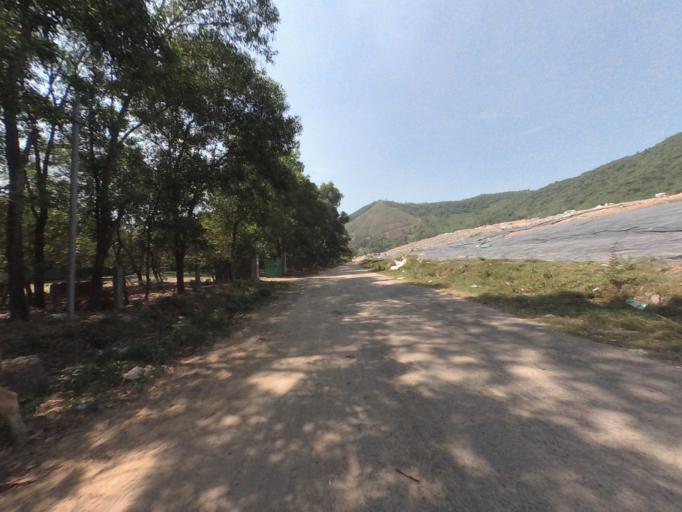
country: VN
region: Da Nang
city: Lien Chieu
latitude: 16.0434
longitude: 108.1426
